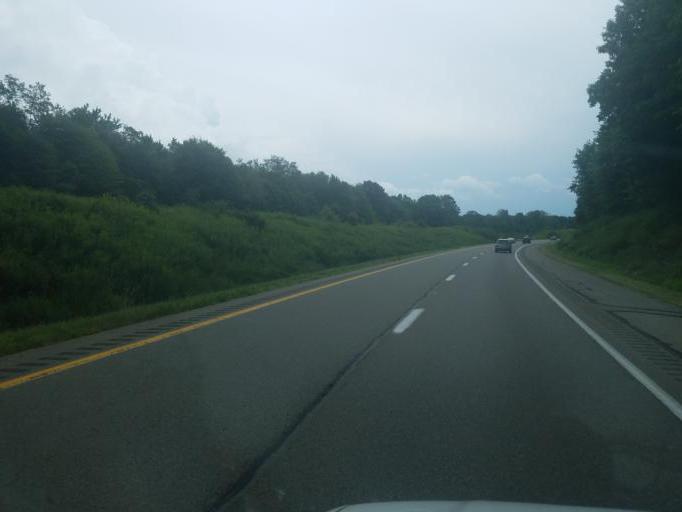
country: US
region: Pennsylvania
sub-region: Crawford County
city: Meadville
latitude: 41.5260
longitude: -80.1705
